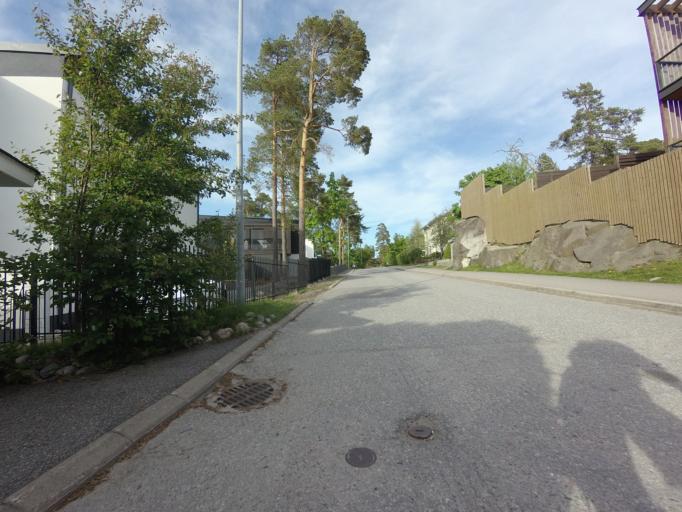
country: FI
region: Uusimaa
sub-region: Helsinki
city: Koukkuniemi
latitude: 60.1460
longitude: 24.7343
